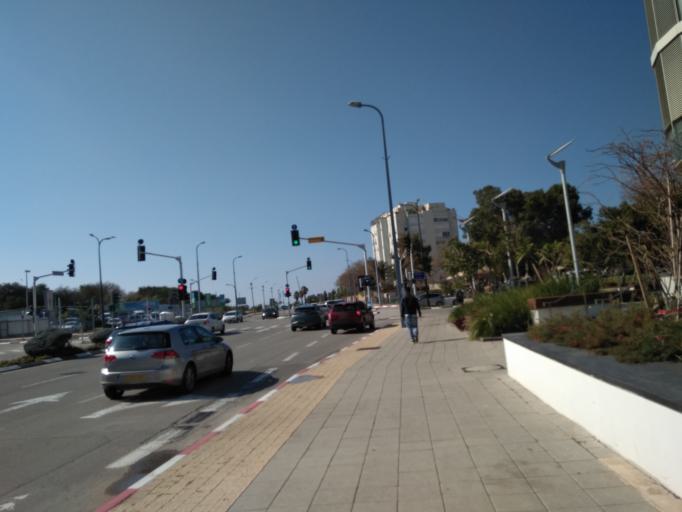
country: IL
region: Tel Aviv
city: Herzliya Pituah
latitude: 32.1630
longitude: 34.8068
